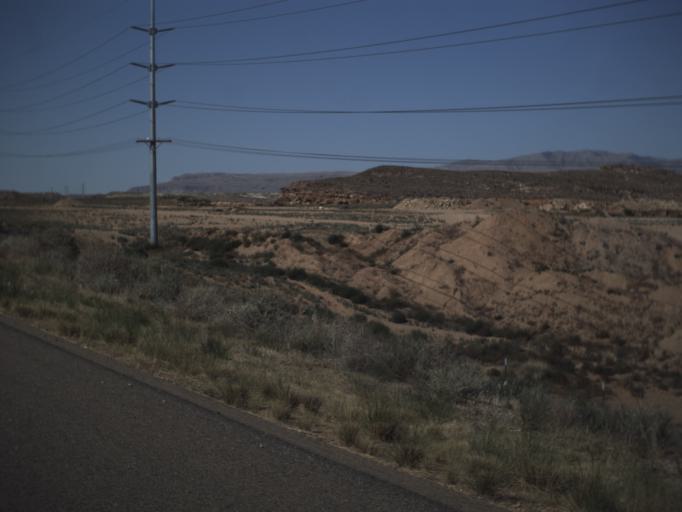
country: US
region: Utah
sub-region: Washington County
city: Saint George
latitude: 37.0081
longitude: -113.5169
